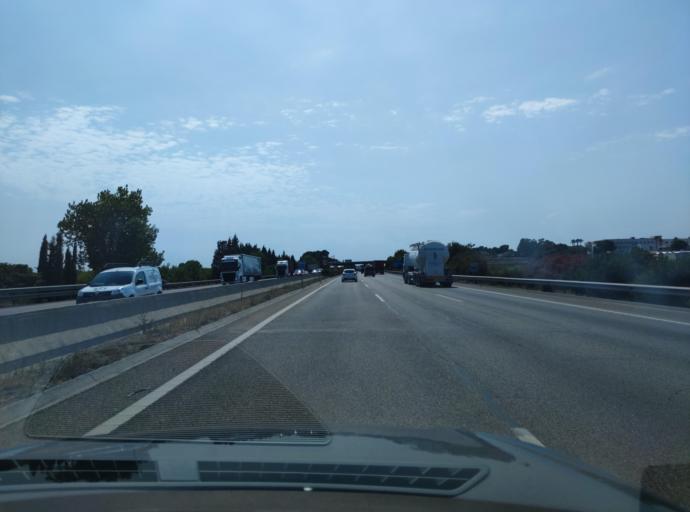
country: ES
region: Valencia
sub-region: Provincia de Valencia
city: Alfara del Patriarca
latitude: 39.5876
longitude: -0.3895
